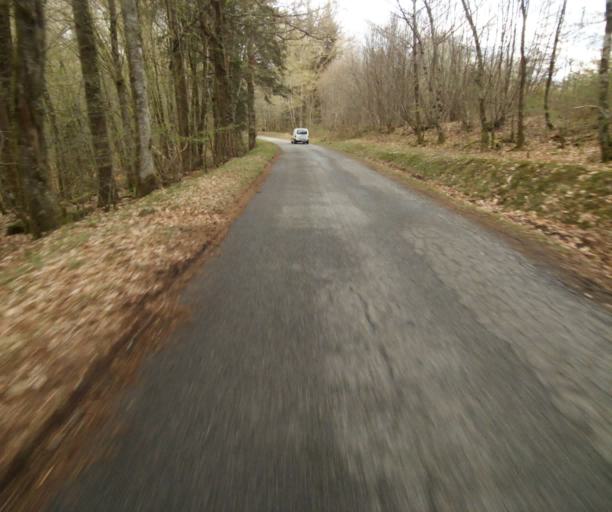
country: FR
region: Limousin
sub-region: Departement de la Correze
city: Argentat
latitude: 45.2252
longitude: 1.9788
